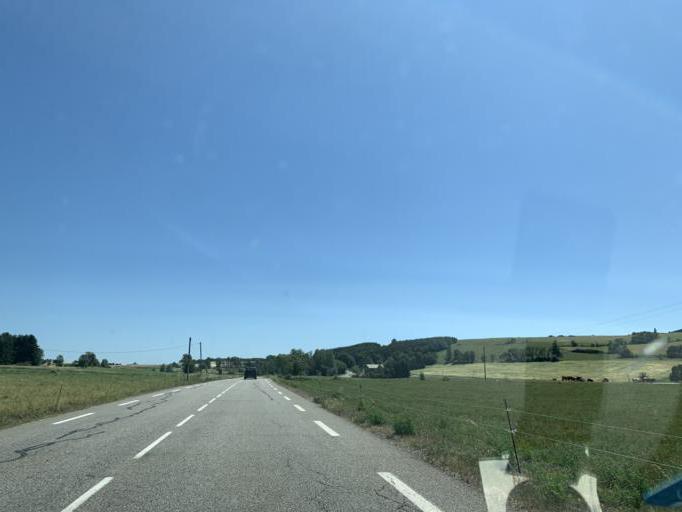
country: FR
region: Provence-Alpes-Cote d'Azur
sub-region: Departement des Hautes-Alpes
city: Saint-Bonnet-en-Champsaur
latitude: 44.6253
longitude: 6.1366
